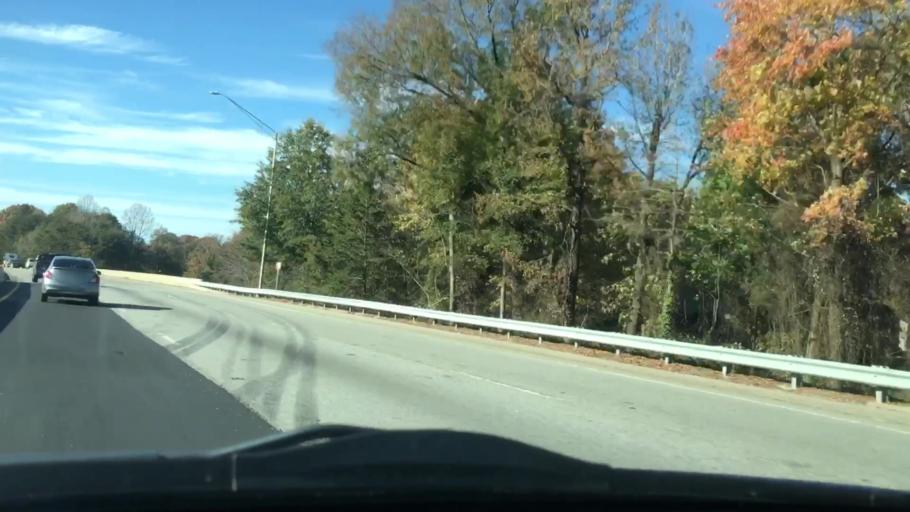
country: US
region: North Carolina
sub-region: Guilford County
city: High Point
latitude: 36.0043
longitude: -79.9948
